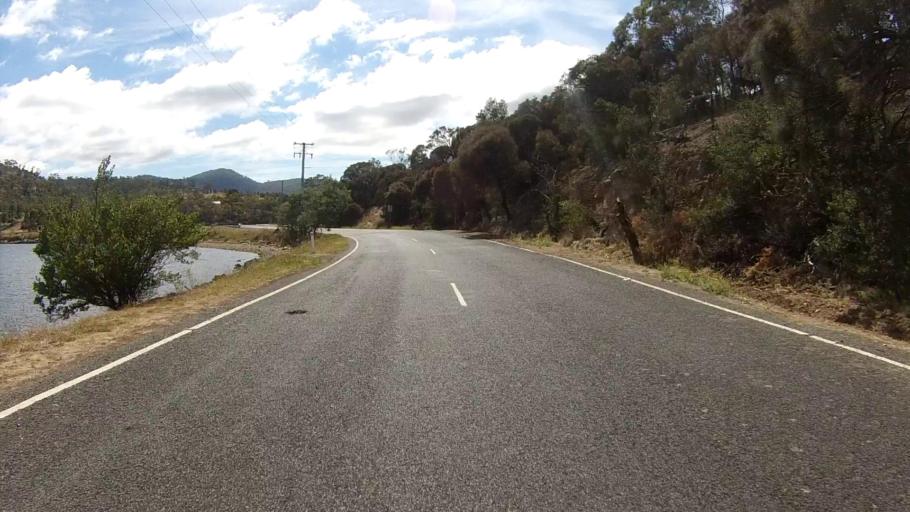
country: AU
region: Tasmania
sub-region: Glenorchy
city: Lutana
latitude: -42.8194
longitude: 147.3199
